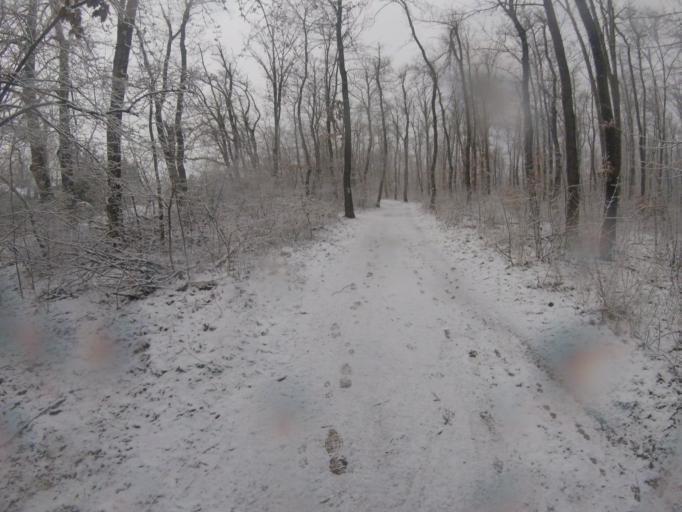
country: HU
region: Pest
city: Solymar
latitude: 47.5841
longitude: 18.9082
